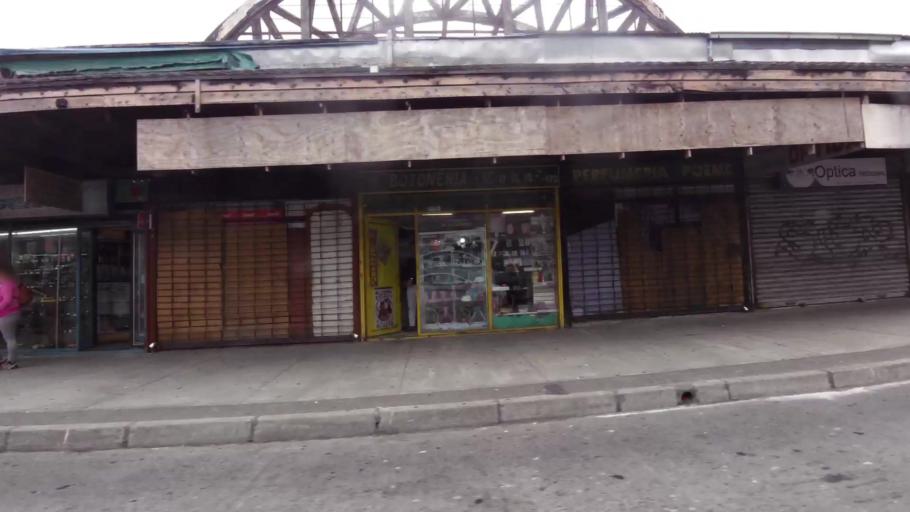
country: CL
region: Biobio
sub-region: Provincia de Concepcion
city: Concepcion
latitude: -36.8259
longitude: -73.0534
